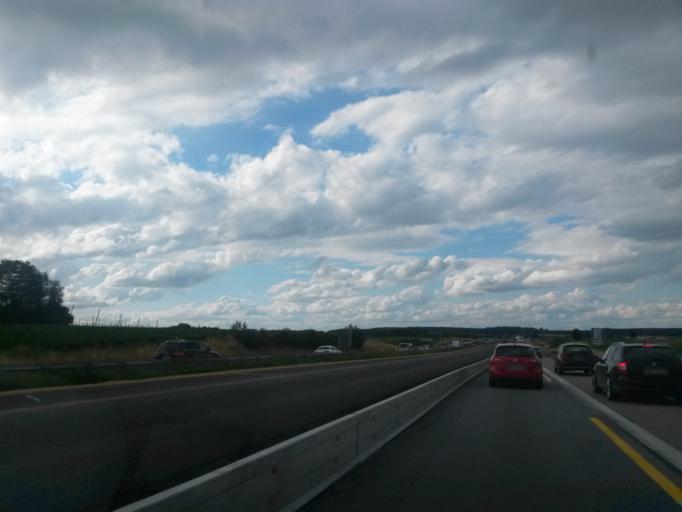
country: DE
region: Bavaria
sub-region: Upper Bavaria
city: Schweitenkirchen
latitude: 48.5387
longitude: 11.5952
